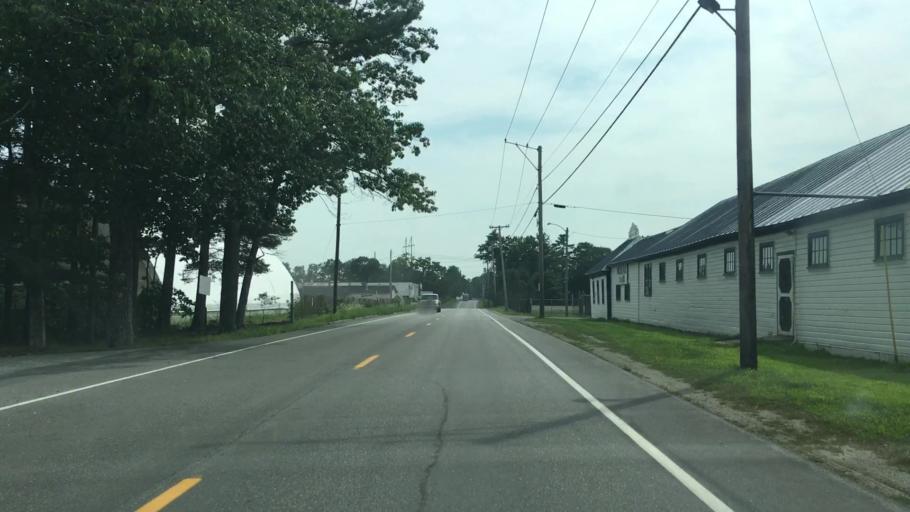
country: US
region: Maine
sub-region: Kennebec County
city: Windsor
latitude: 44.2845
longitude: -69.5944
